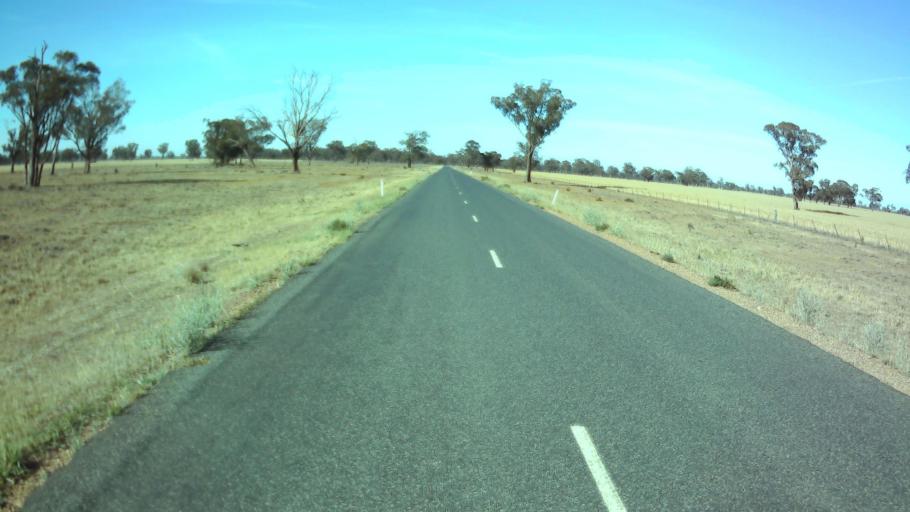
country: AU
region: New South Wales
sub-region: Weddin
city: Grenfell
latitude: -34.0520
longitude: 147.9181
